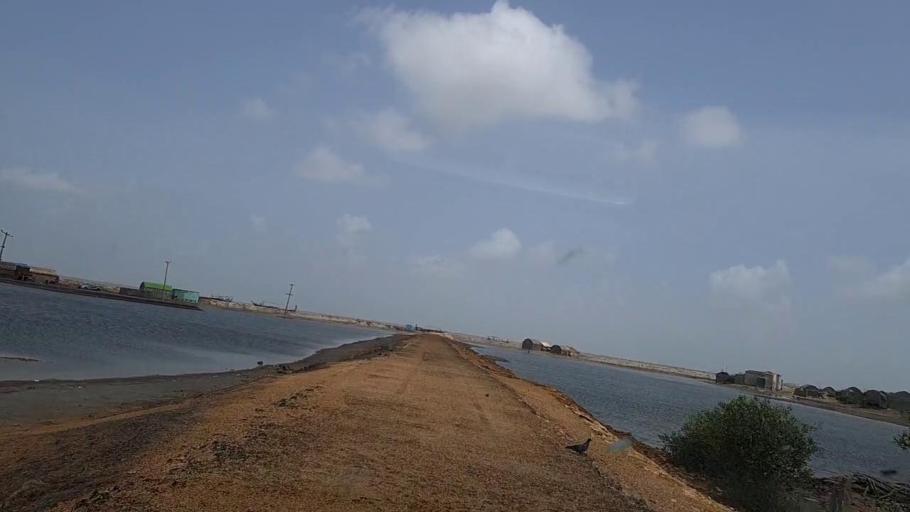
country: PK
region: Sindh
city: Keti Bandar
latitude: 24.1282
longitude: 67.4675
